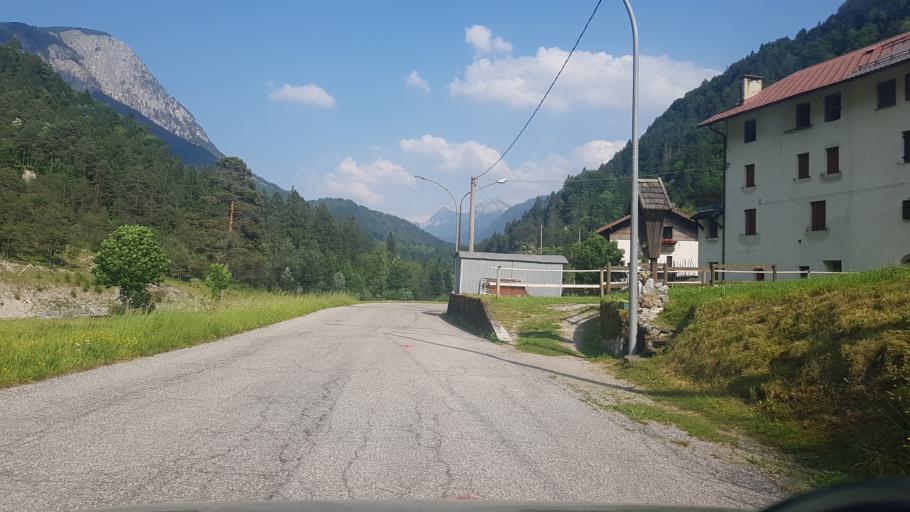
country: IT
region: Friuli Venezia Giulia
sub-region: Provincia di Udine
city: Pontebba
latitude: 46.5204
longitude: 13.2764
